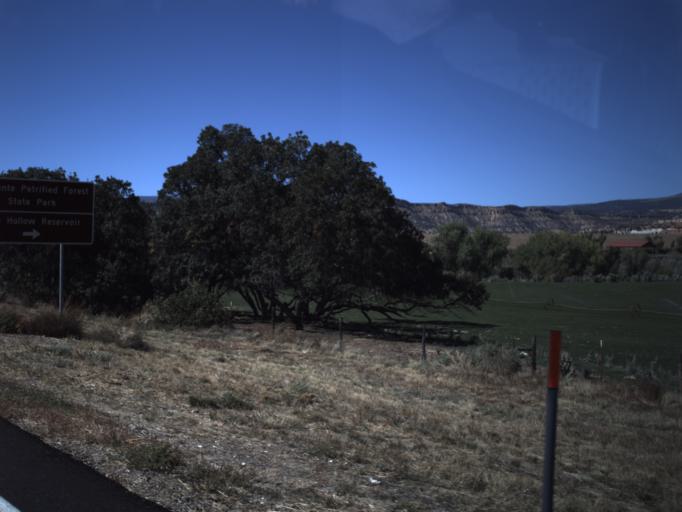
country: US
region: Utah
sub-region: Wayne County
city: Loa
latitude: 37.7775
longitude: -111.6267
